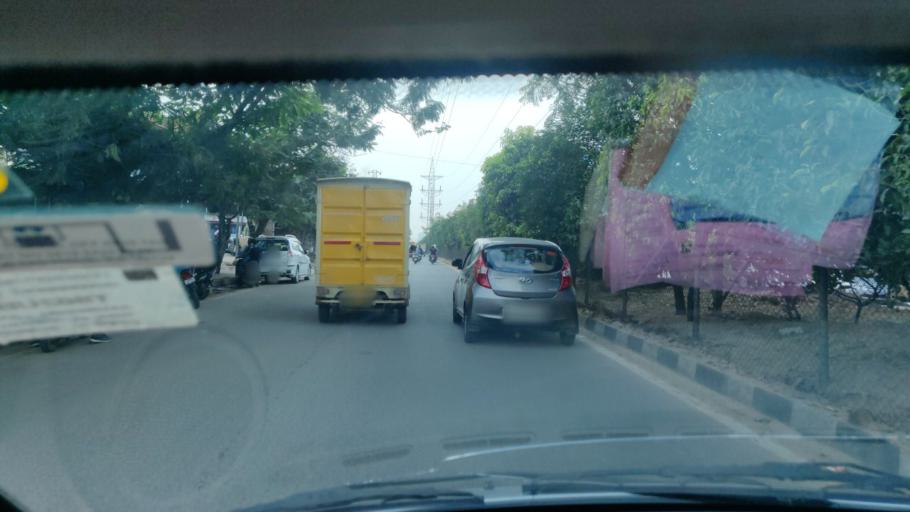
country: IN
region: Telangana
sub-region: Rangareddi
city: Kukatpalli
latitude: 17.4519
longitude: 78.3913
